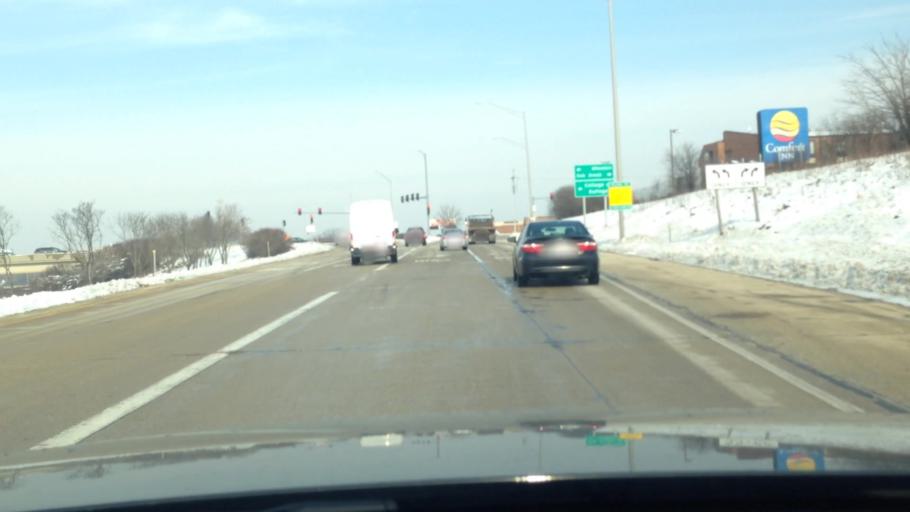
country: US
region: Illinois
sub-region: DuPage County
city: Downers Grove
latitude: 41.8317
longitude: -88.0279
